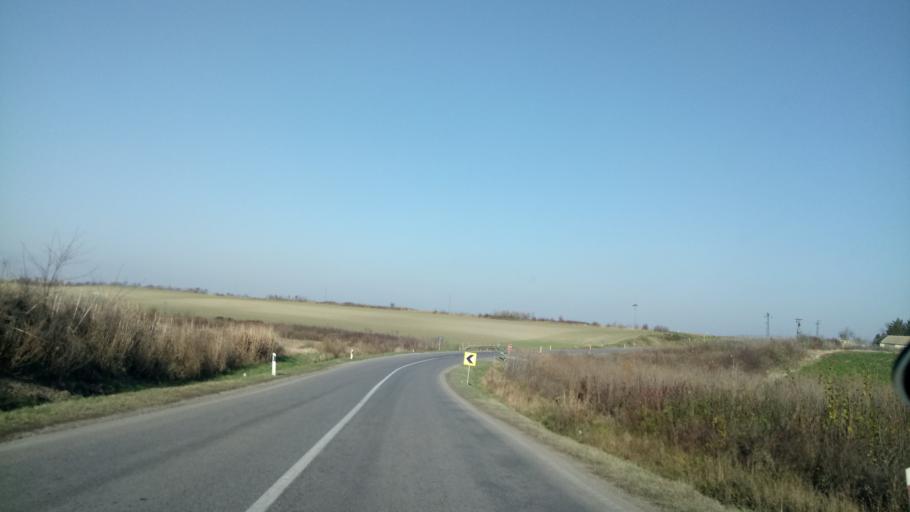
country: RS
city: Ljukovo
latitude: 45.0274
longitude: 20.0465
